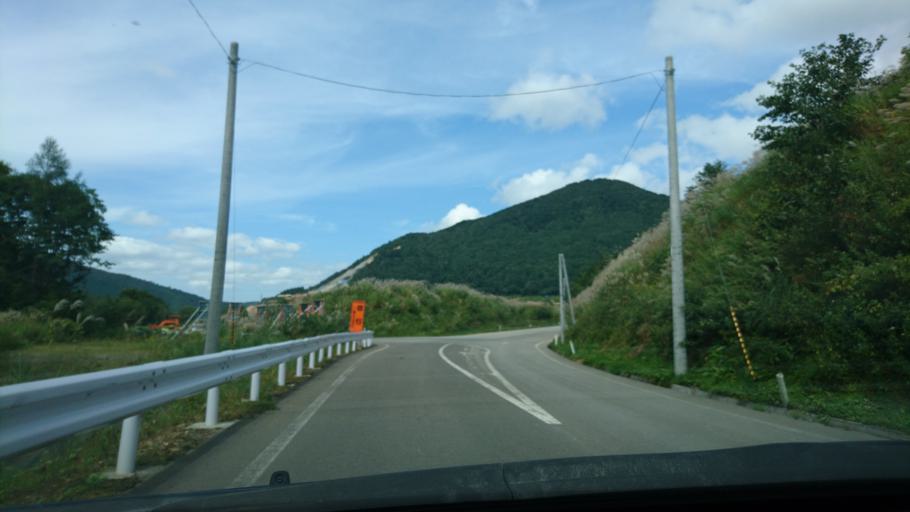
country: JP
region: Akita
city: Yuzawa
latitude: 39.0301
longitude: 140.7277
